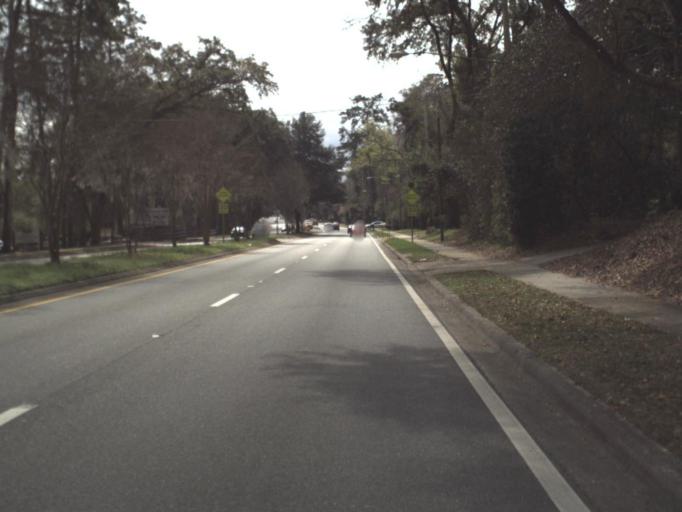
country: US
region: Florida
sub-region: Leon County
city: Tallahassee
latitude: 30.4739
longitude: -84.2645
